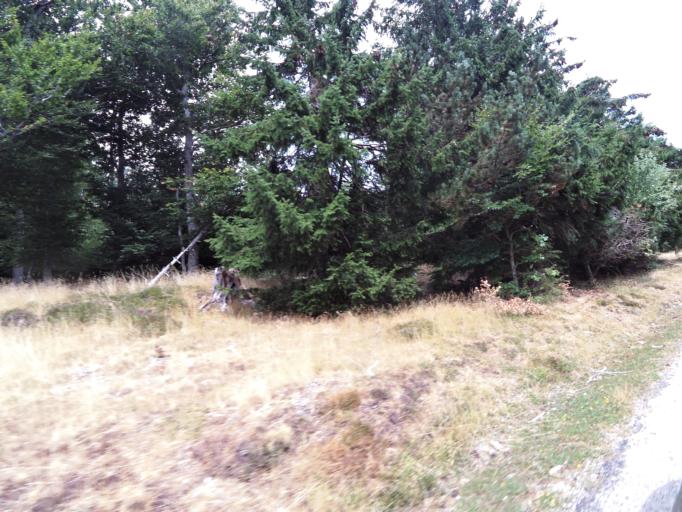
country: FR
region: Languedoc-Roussillon
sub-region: Departement du Gard
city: Valleraugue
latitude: 44.0678
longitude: 3.5947
